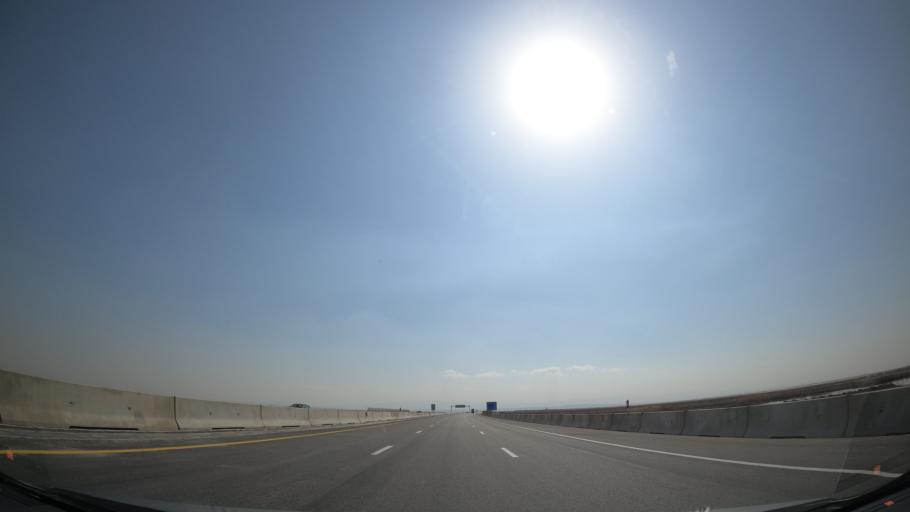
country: IR
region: Qazvin
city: Abyek
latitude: 35.9502
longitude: 50.4673
